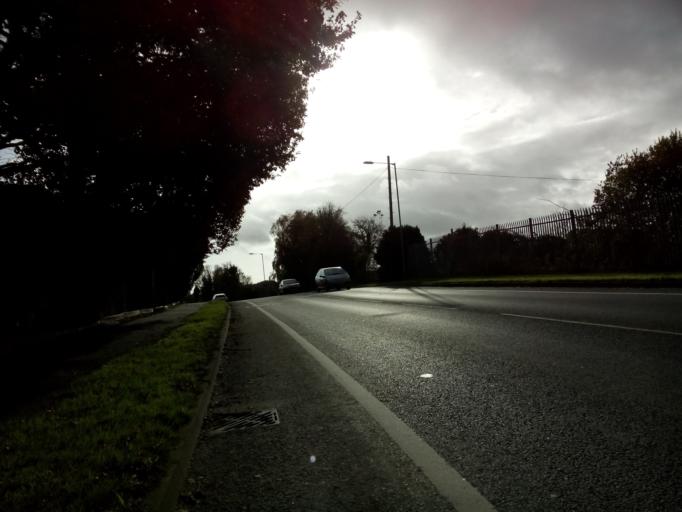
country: GB
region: England
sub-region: Suffolk
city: Ipswich
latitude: 52.0436
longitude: 1.1658
